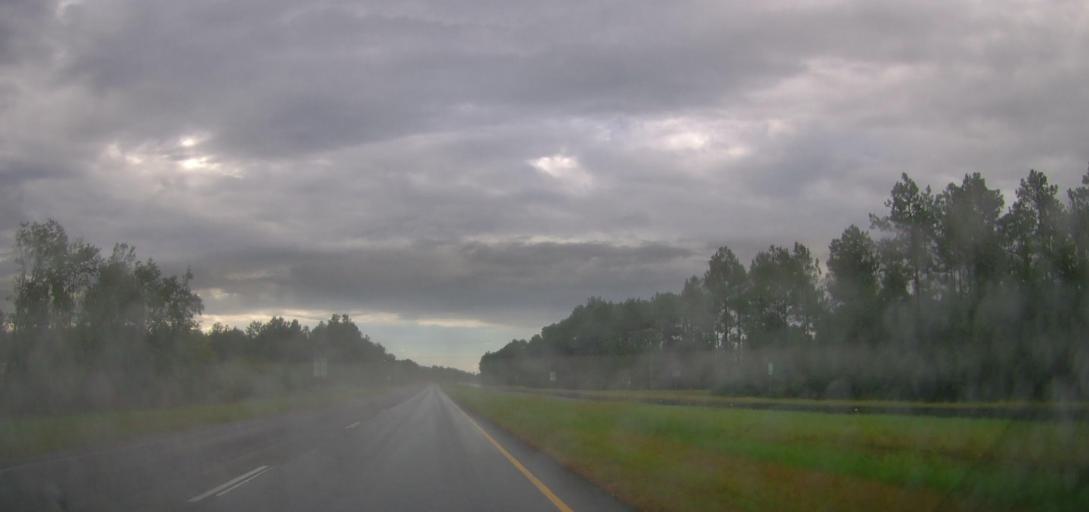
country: US
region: Georgia
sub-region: Ware County
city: Deenwood
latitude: 31.2117
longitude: -82.4169
